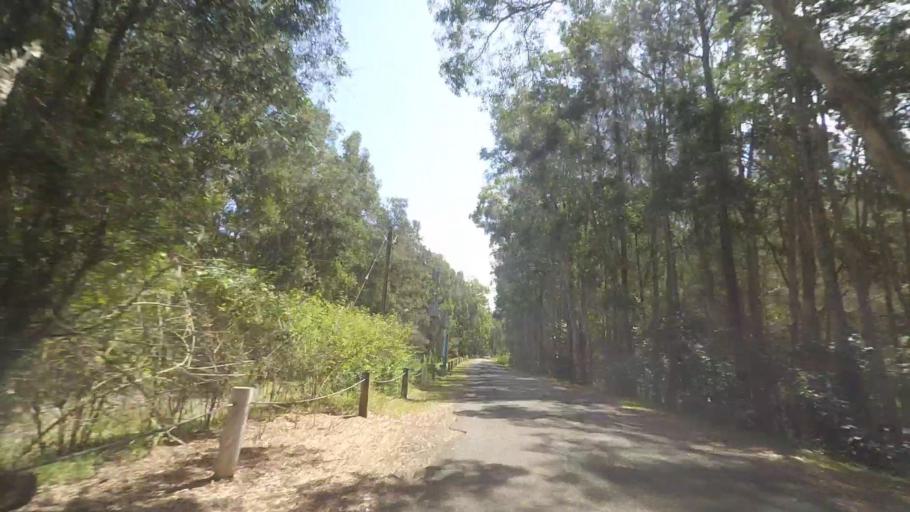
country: AU
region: New South Wales
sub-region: Great Lakes
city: Bulahdelah
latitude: -32.5082
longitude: 152.3007
